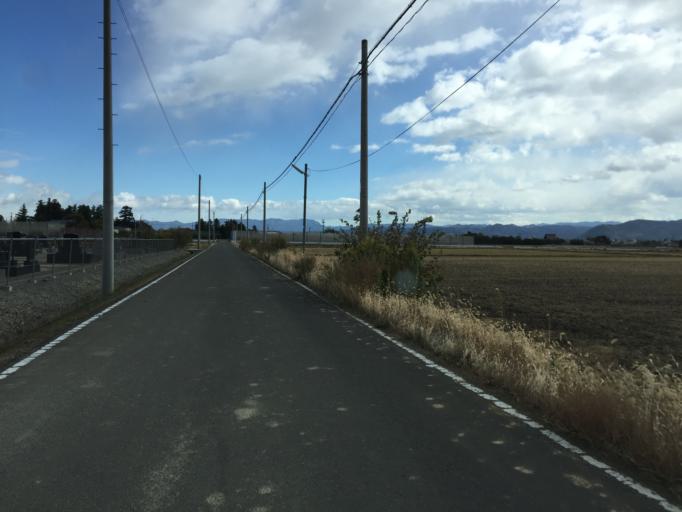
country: JP
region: Fukushima
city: Fukushima-shi
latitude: 37.8088
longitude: 140.4271
